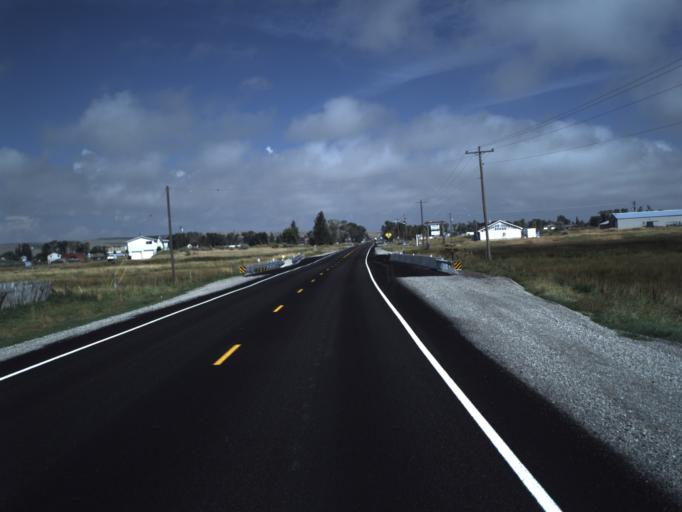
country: US
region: Utah
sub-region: Rich County
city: Randolph
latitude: 41.6536
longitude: -111.1848
